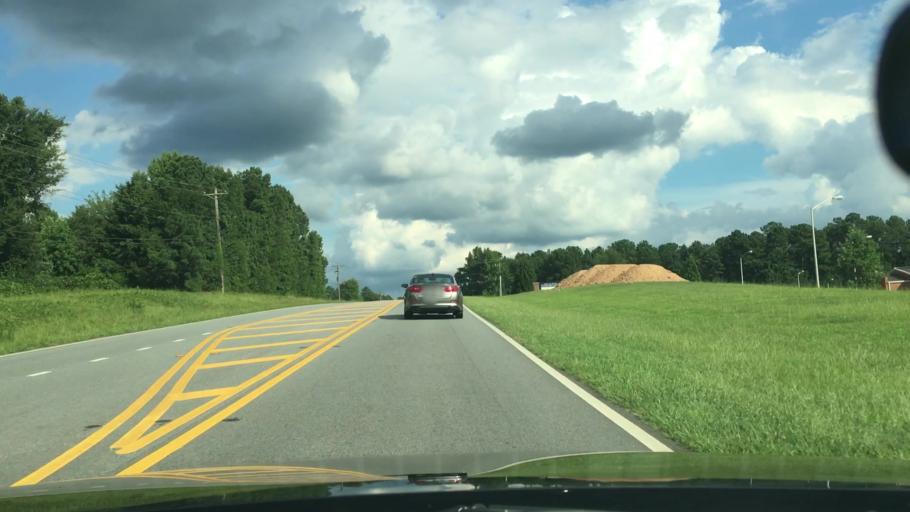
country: US
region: Georgia
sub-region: Coweta County
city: East Newnan
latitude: 33.3442
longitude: -84.6901
